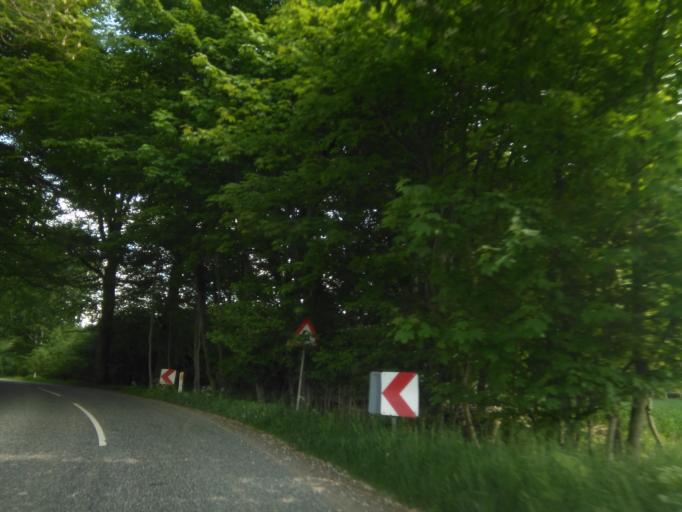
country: DK
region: Central Jutland
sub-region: Favrskov Kommune
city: Hammel
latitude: 56.2372
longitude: 9.9343
